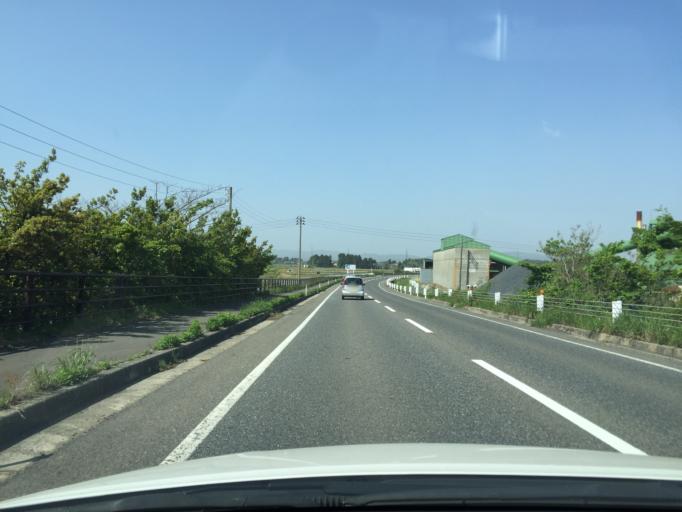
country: JP
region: Niigata
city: Gosen
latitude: 37.7492
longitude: 139.2177
